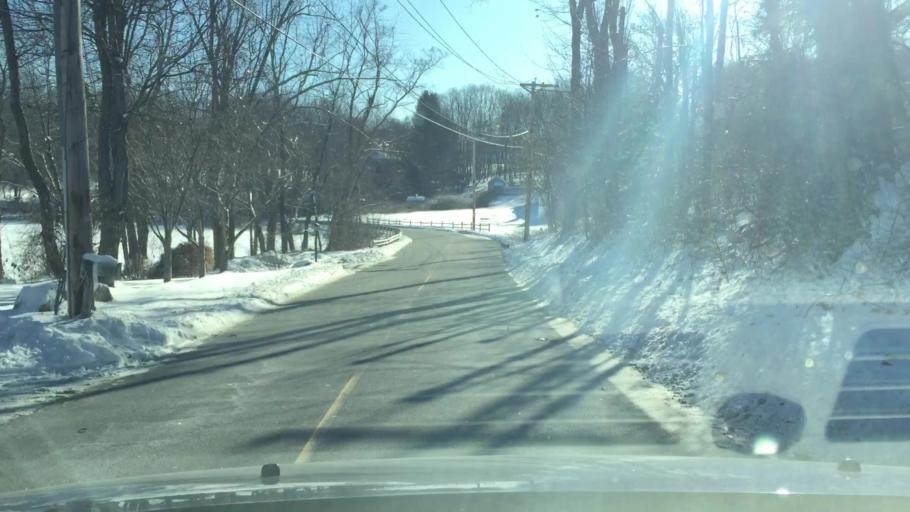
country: US
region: Massachusetts
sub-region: Essex County
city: North Andover
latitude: 42.6908
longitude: -71.1102
